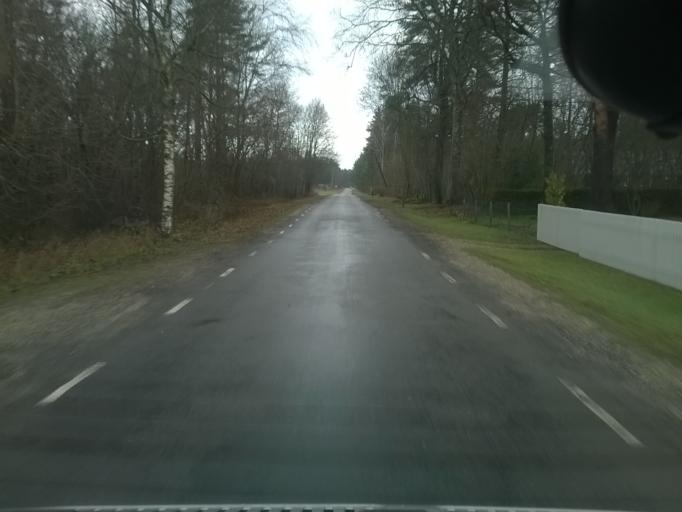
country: EE
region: Laeaene
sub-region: Ridala Parish
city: Uuemoisa
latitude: 58.9518
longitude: 23.7252
